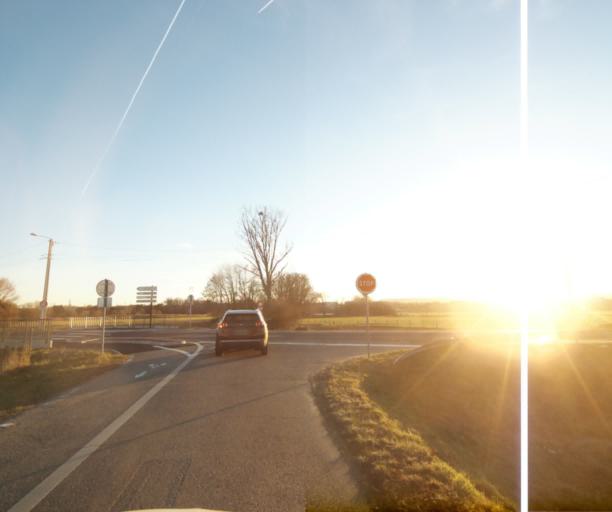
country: FR
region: Lorraine
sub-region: Departement de Meurthe-et-Moselle
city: Laneuveville-devant-Nancy
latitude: 48.6634
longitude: 6.2378
